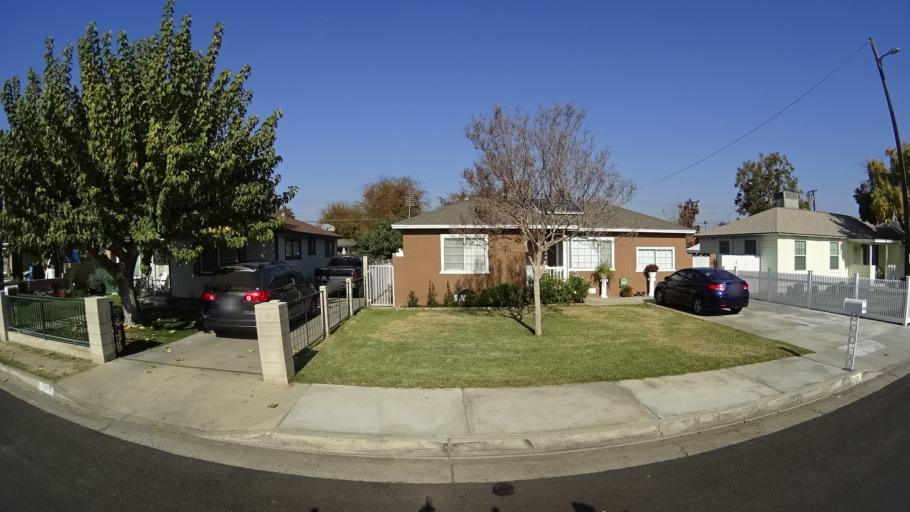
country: US
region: California
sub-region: Kern County
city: Bakersfield
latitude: 35.3431
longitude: -119.0333
